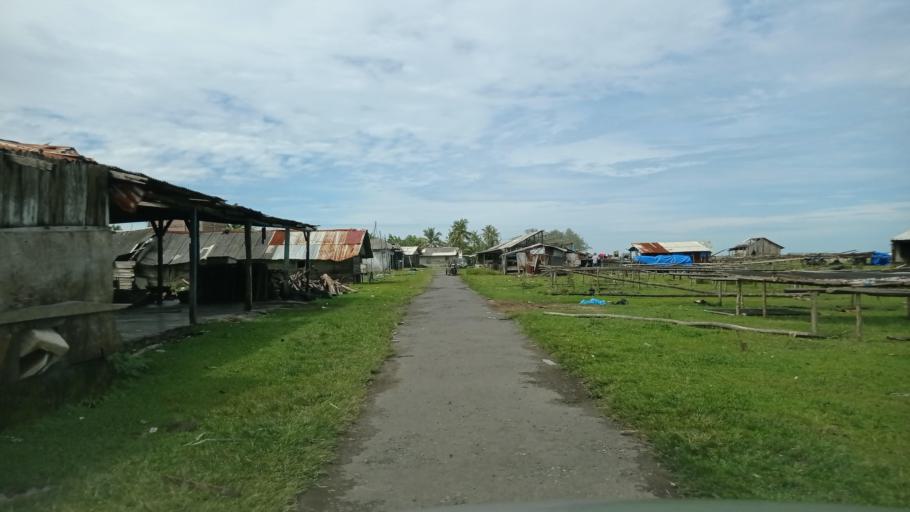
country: ID
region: Bengkulu
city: Ipuh
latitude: -2.5870
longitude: 101.1122
